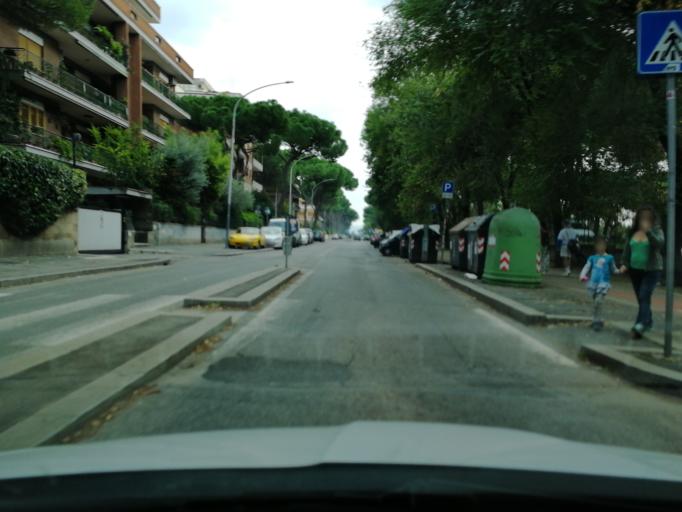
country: IT
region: Latium
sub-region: Citta metropolitana di Roma Capitale
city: Rome
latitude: 41.8522
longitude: 12.5592
